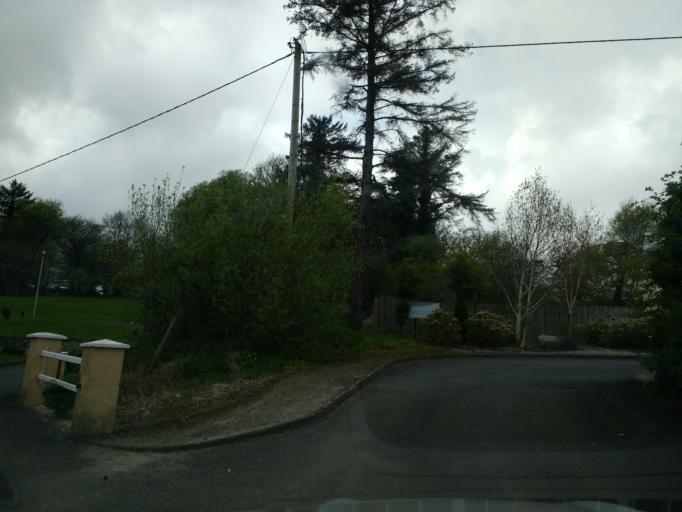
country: IE
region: Ulster
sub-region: County Donegal
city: Buncrana
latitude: 55.0979
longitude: -7.5365
